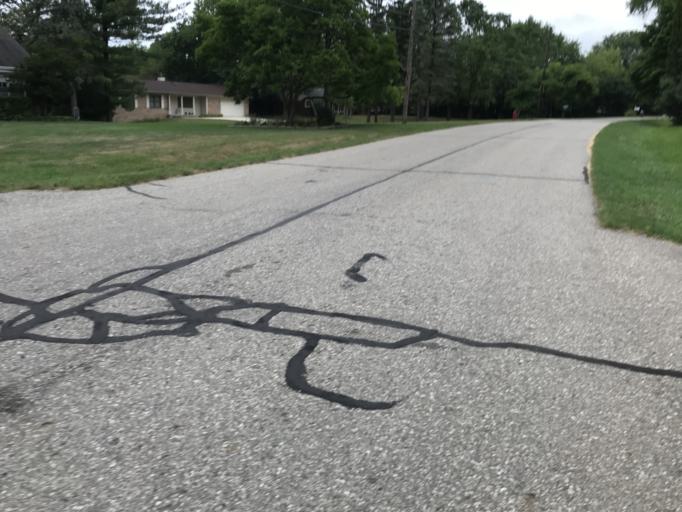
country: US
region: Michigan
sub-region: Oakland County
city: Farmington
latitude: 42.4730
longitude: -83.3314
